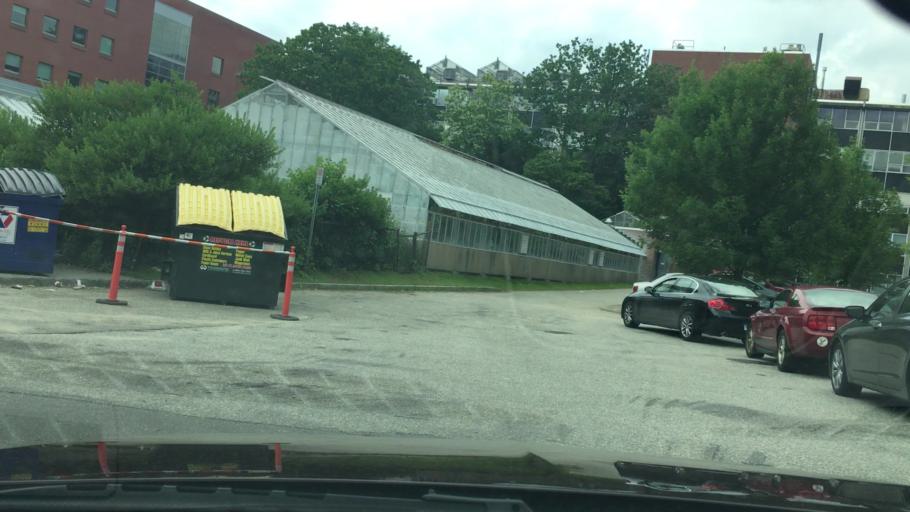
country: US
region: Connecticut
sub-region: Tolland County
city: Storrs
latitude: 41.8098
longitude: -72.2554
